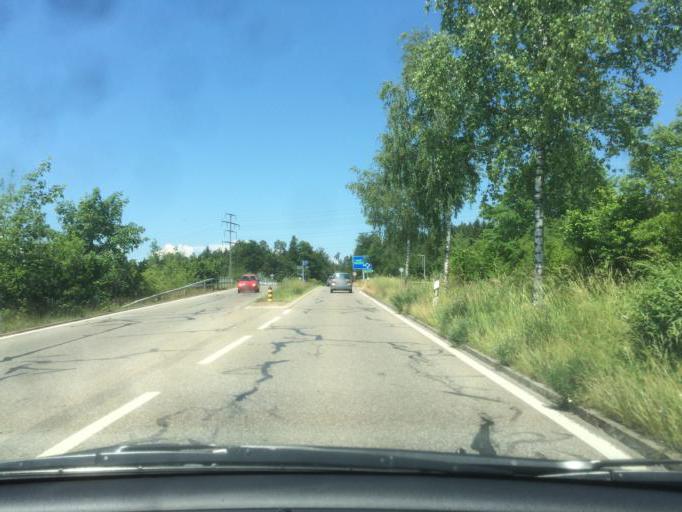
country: CH
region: Zurich
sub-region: Bezirk Uster
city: Uster / Gschwader
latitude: 47.3676
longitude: 8.7118
